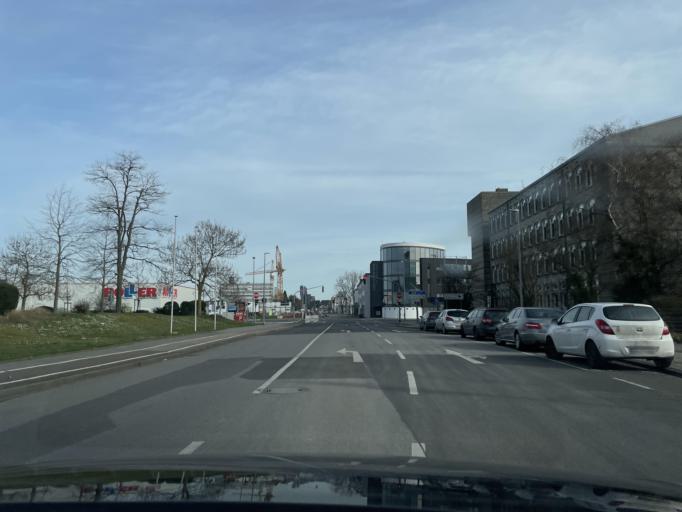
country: DE
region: North Rhine-Westphalia
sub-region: Regierungsbezirk Dusseldorf
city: Monchengladbach
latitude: 51.1957
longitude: 6.4511
